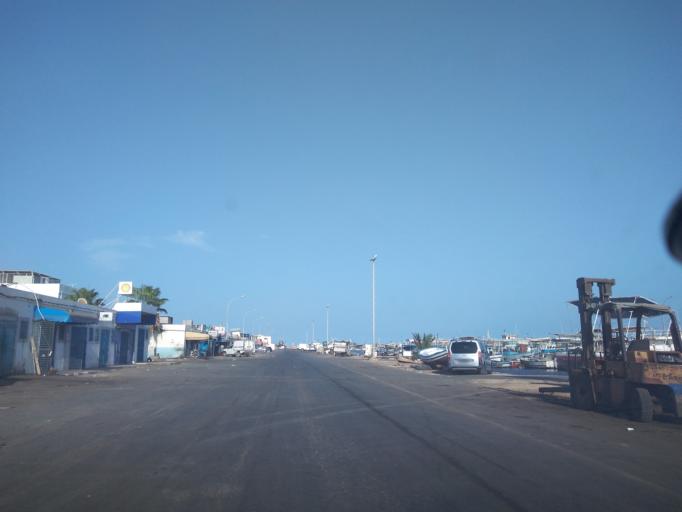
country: TN
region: Safaqis
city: Sfax
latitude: 34.7131
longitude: 10.7613
